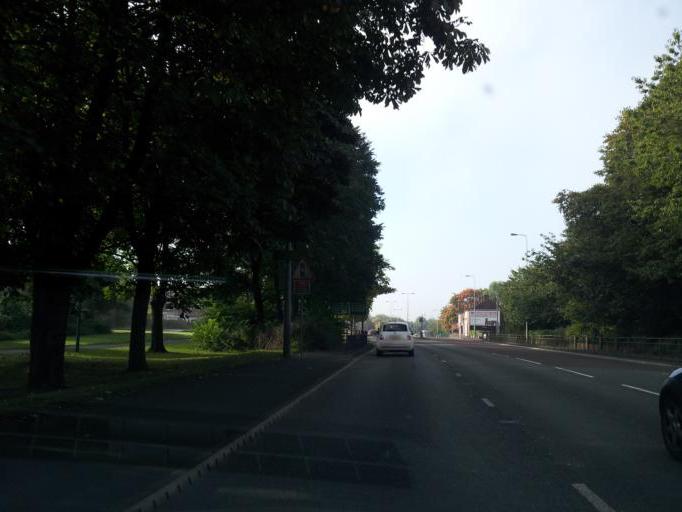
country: GB
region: England
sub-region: Borough of Oldham
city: Oldham
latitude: 53.5477
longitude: -2.1450
